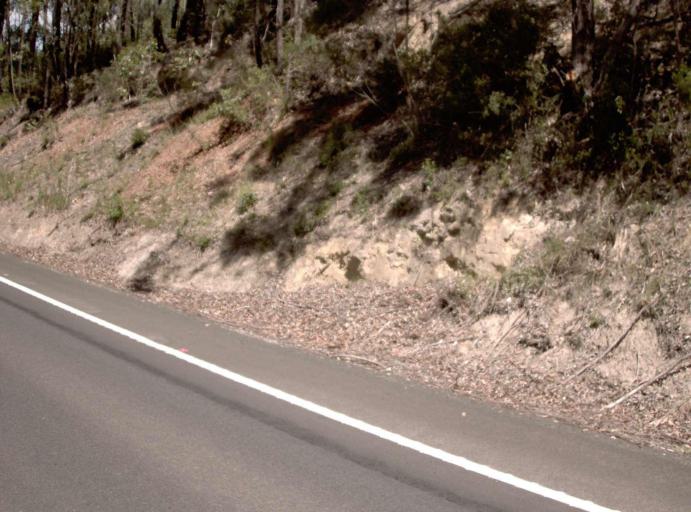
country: AU
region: New South Wales
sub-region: Bombala
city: Bombala
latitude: -37.5646
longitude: 149.0583
